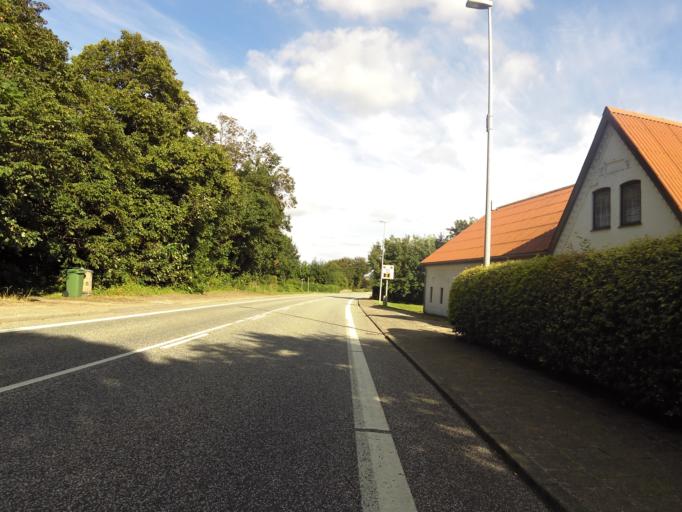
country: DK
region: South Denmark
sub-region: Haderslev Kommune
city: Gram
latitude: 55.2284
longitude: 8.9913
